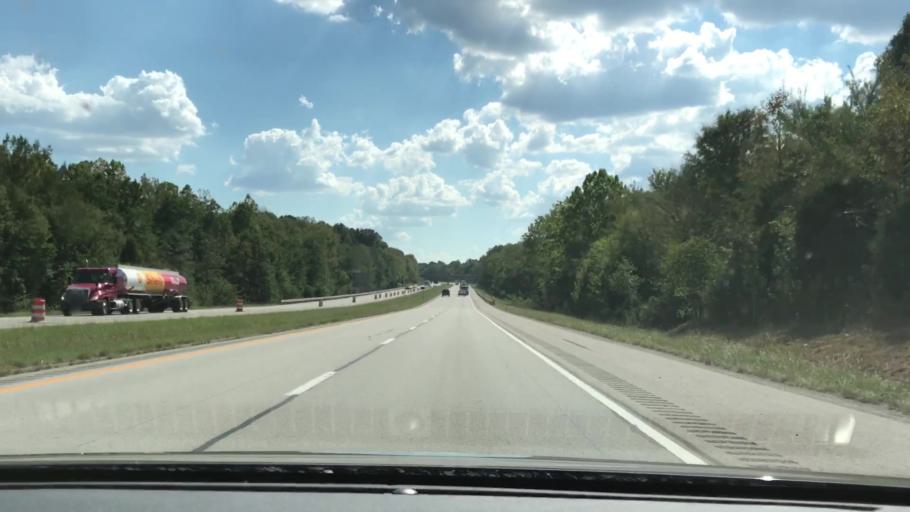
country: US
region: Kentucky
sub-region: Ohio County
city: Oak Grove
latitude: 37.2736
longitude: -86.7463
